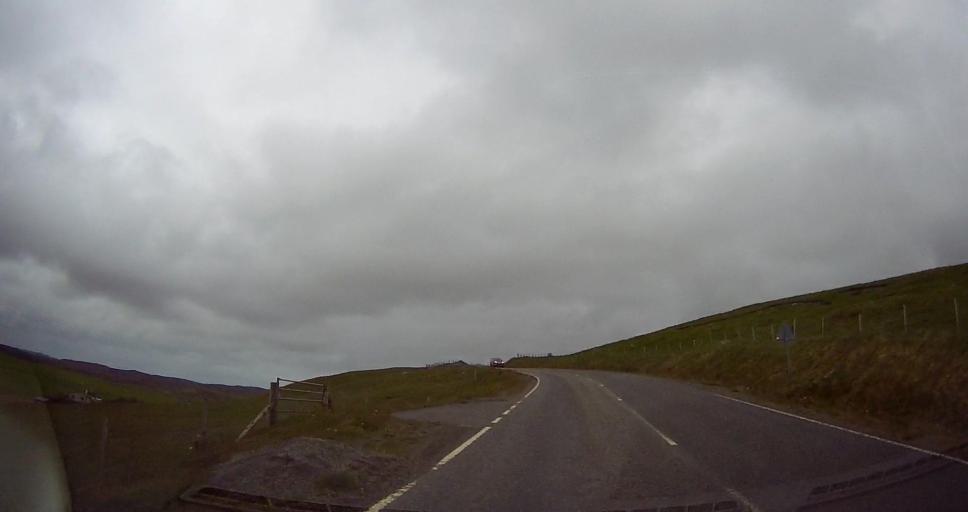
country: GB
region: Scotland
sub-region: Shetland Islands
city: Lerwick
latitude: 60.2564
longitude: -1.4075
